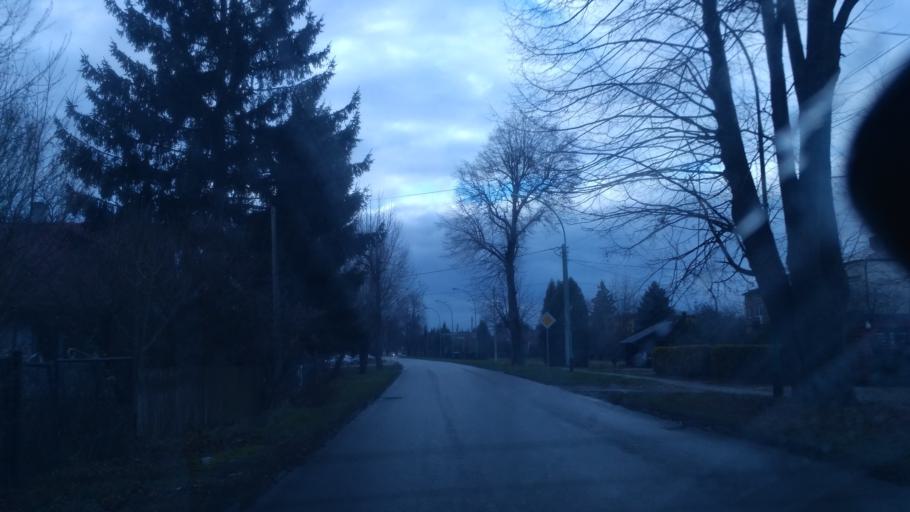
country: PL
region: Subcarpathian Voivodeship
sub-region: Powiat lancucki
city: Lancut
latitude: 50.0908
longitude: 22.2445
